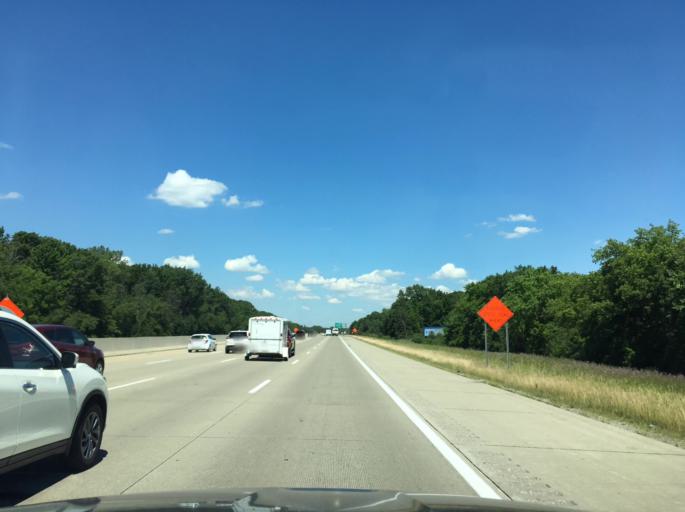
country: US
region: Michigan
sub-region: Saginaw County
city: Bridgeport
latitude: 43.3262
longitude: -83.8535
